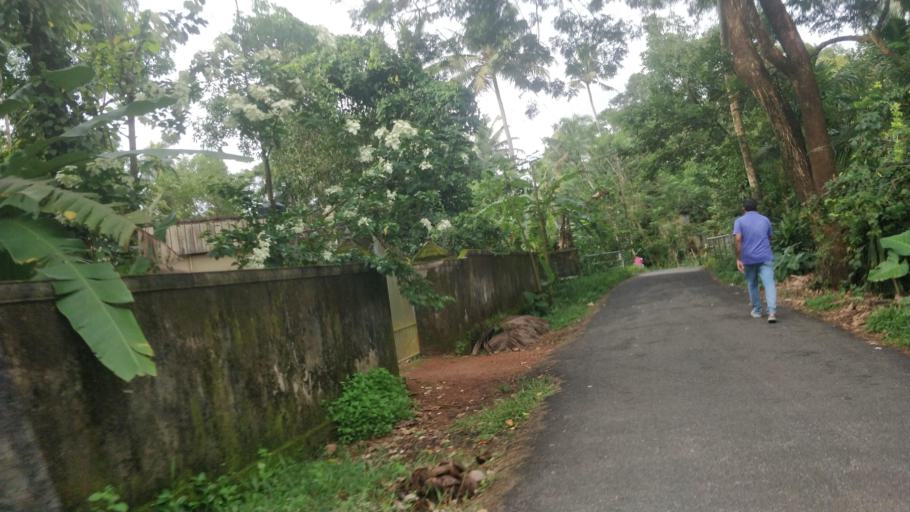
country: IN
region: Kerala
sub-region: Alappuzha
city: Shertallai
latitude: 9.6897
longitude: 76.3593
